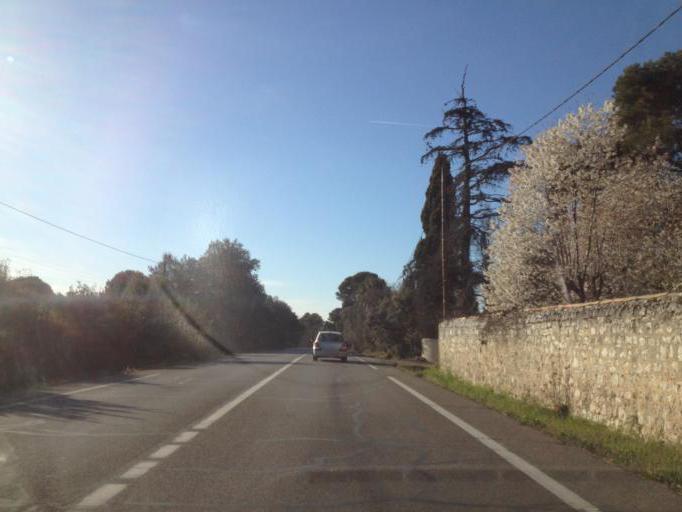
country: FR
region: Provence-Alpes-Cote d'Azur
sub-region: Departement des Bouches-du-Rhone
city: Eguilles
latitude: 43.5981
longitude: 5.3497
